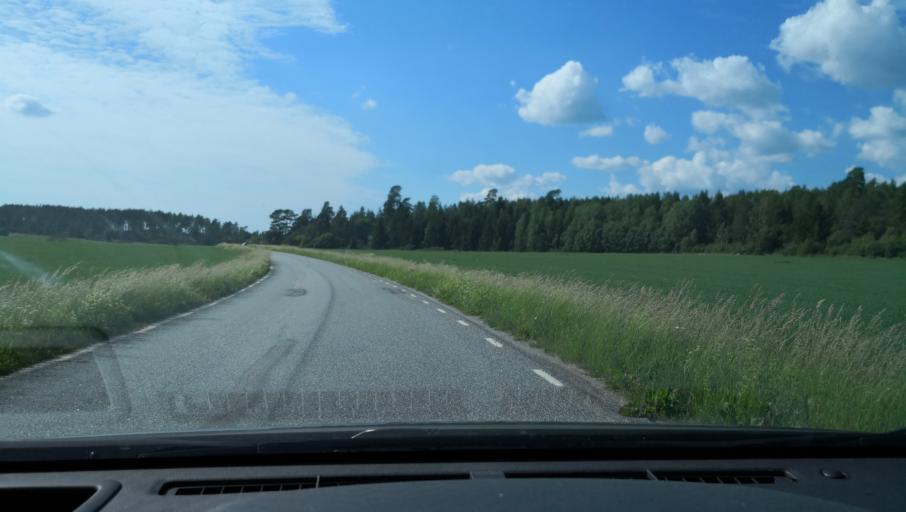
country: SE
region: Uppsala
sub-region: Enkopings Kommun
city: Orsundsbro
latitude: 59.8388
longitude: 17.2965
